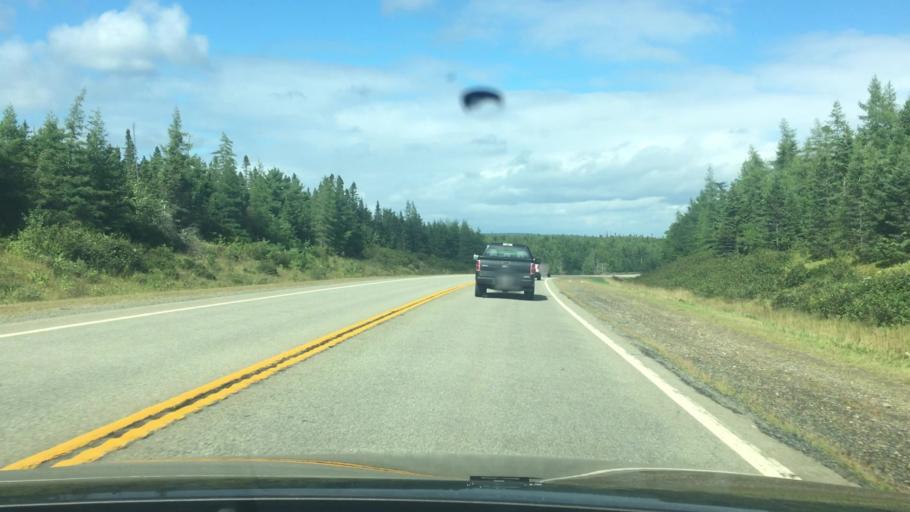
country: CA
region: Nova Scotia
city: Princeville
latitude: 45.6236
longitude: -61.0475
